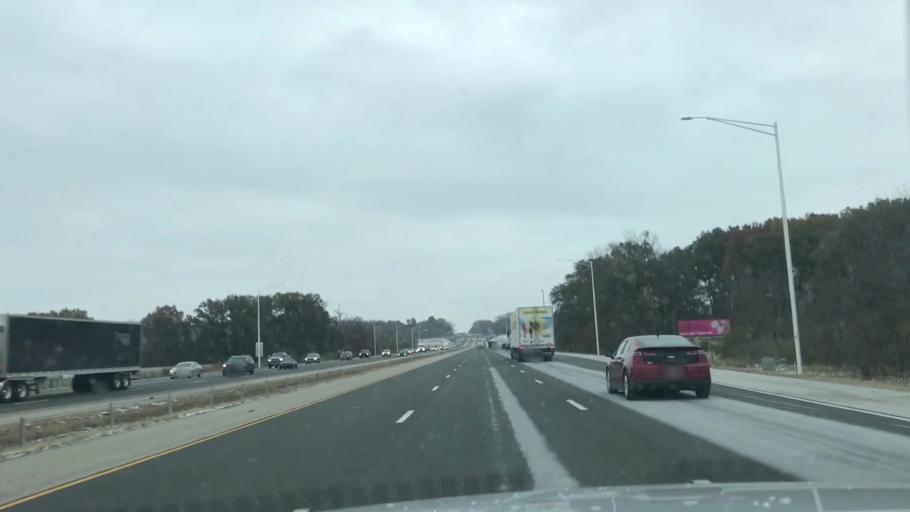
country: US
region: Illinois
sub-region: Madison County
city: Glen Carbon
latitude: 38.7567
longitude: -90.0204
